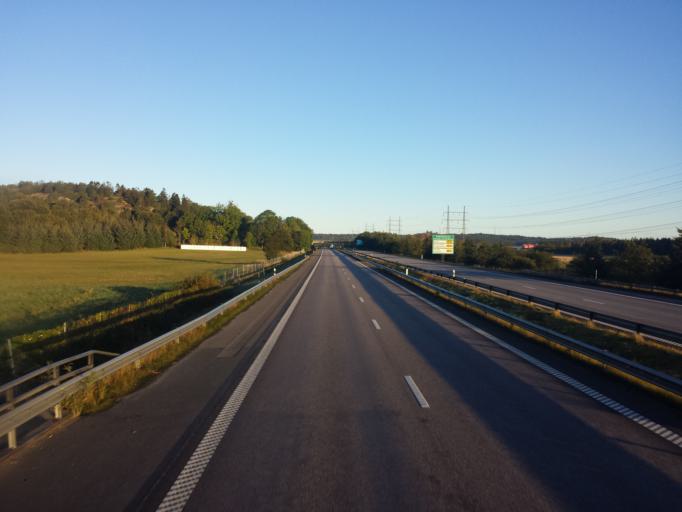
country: SE
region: Halland
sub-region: Kungsbacka Kommun
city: Kungsbacka
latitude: 57.4600
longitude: 12.0815
